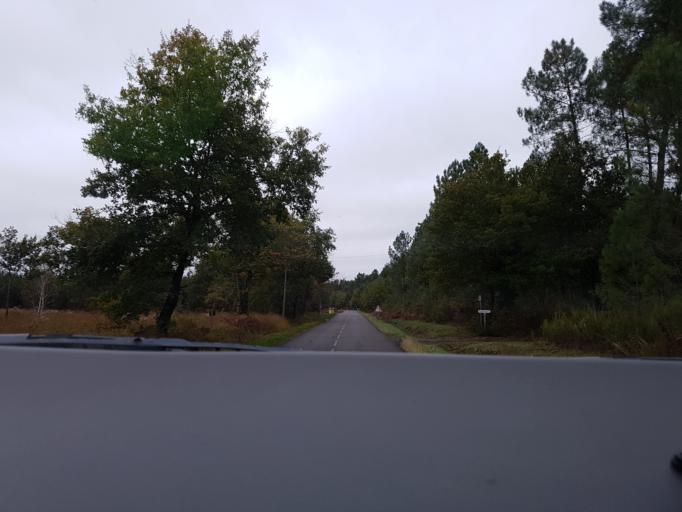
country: FR
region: Aquitaine
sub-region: Departement des Landes
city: Roquefort
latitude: 44.0798
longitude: -0.3777
